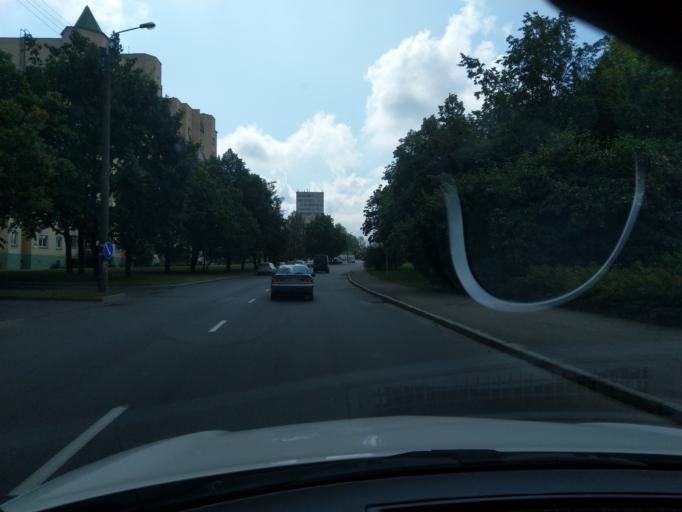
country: BY
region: Minsk
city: Minsk
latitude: 53.8953
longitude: 27.5821
